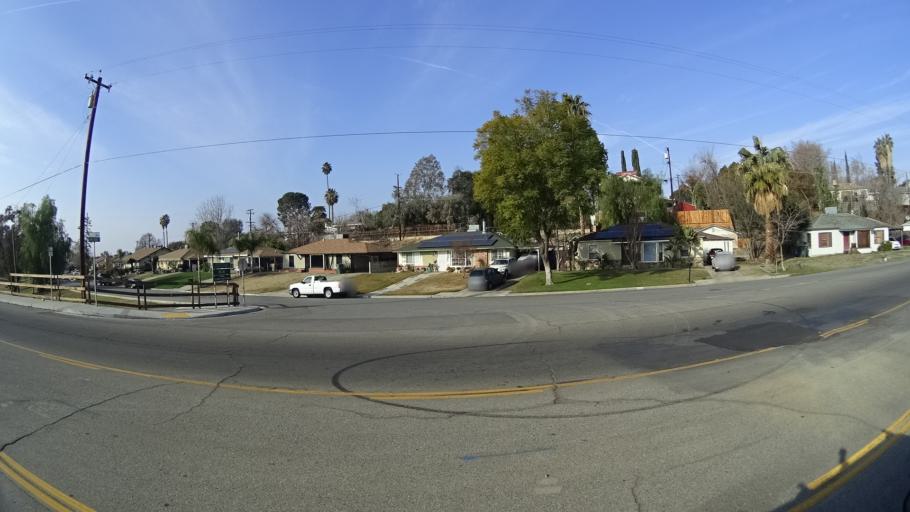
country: US
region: California
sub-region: Kern County
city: Oildale
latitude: 35.4011
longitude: -118.9850
